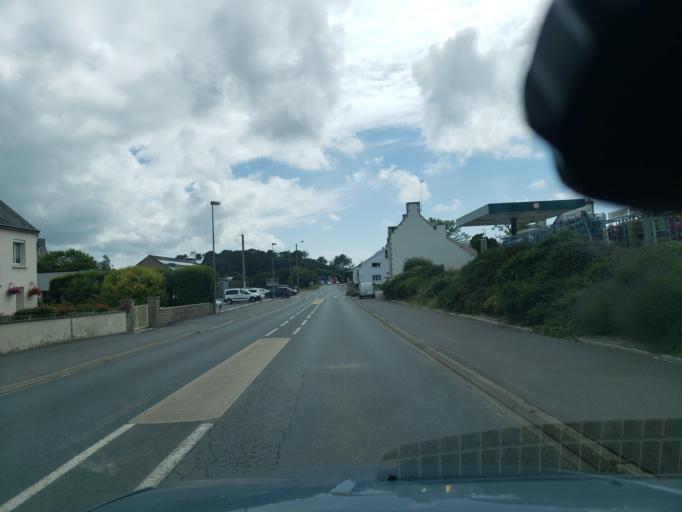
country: FR
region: Brittany
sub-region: Departement du Finistere
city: Ploneour-Lanvern
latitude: 47.9001
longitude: -4.2846
